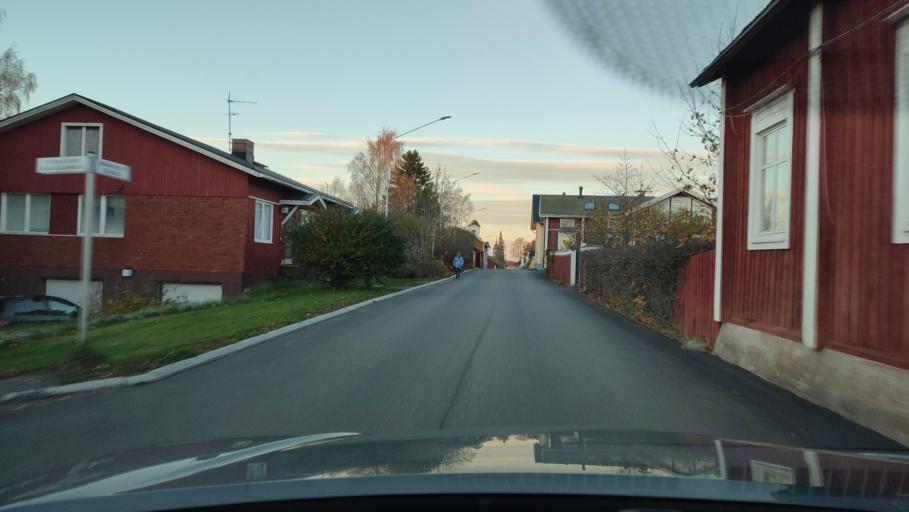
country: FI
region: Ostrobothnia
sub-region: Sydosterbotten
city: Kristinestad
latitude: 62.2712
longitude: 21.3733
